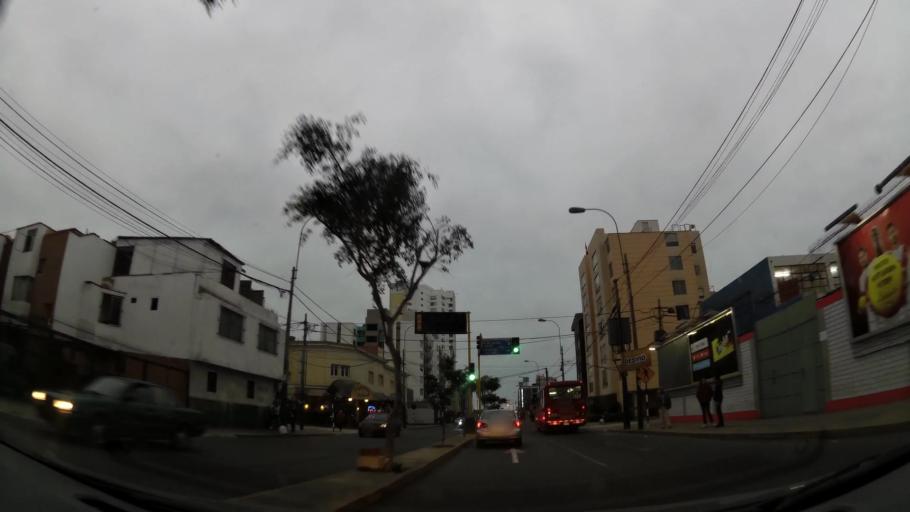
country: PE
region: Lima
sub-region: Lima
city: San Isidro
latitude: -12.0951
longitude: -77.0717
